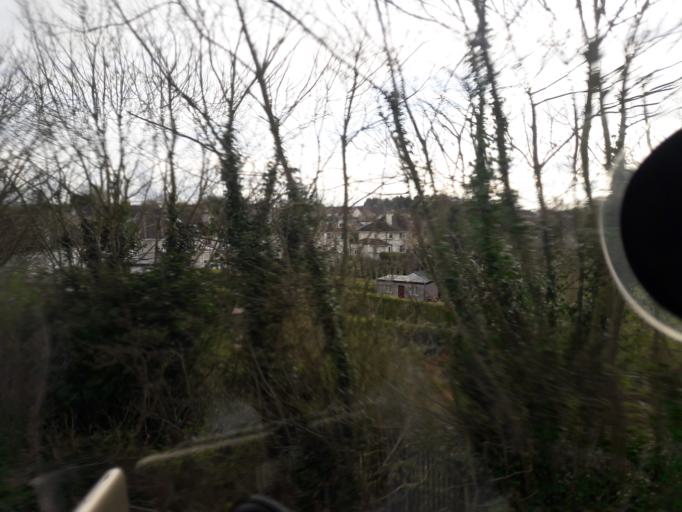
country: IE
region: Leinster
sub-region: An Iarmhi
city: An Muileann gCearr
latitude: 53.5201
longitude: -7.3350
